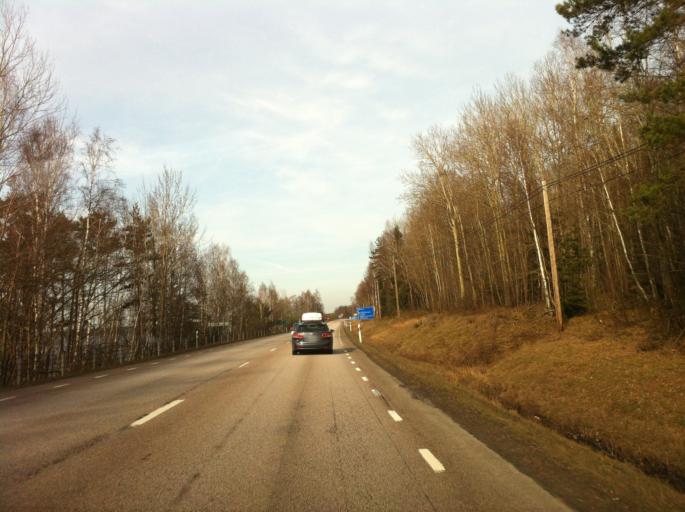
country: SE
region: Vaestra Goetaland
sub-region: Gullspangs Kommun
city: Gullspang
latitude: 59.0475
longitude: 14.1391
